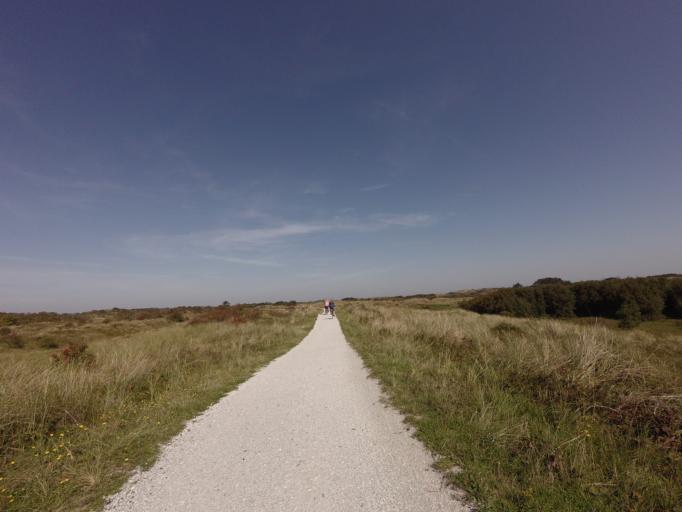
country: NL
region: Friesland
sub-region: Gemeente Schiermonnikoog
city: Schiermonnikoog
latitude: 53.4747
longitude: 6.1404
